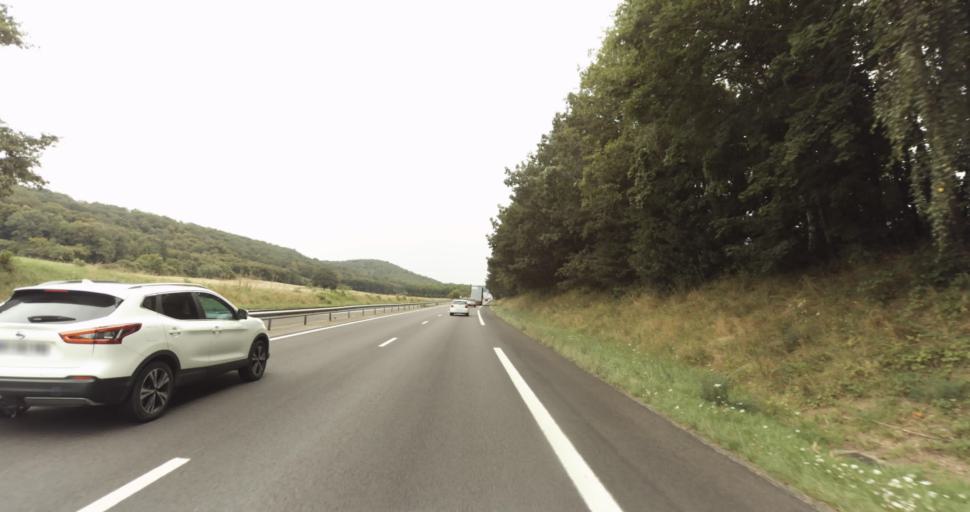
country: FR
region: Haute-Normandie
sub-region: Departement de l'Eure
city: Acquigny
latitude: 49.1734
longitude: 1.1700
